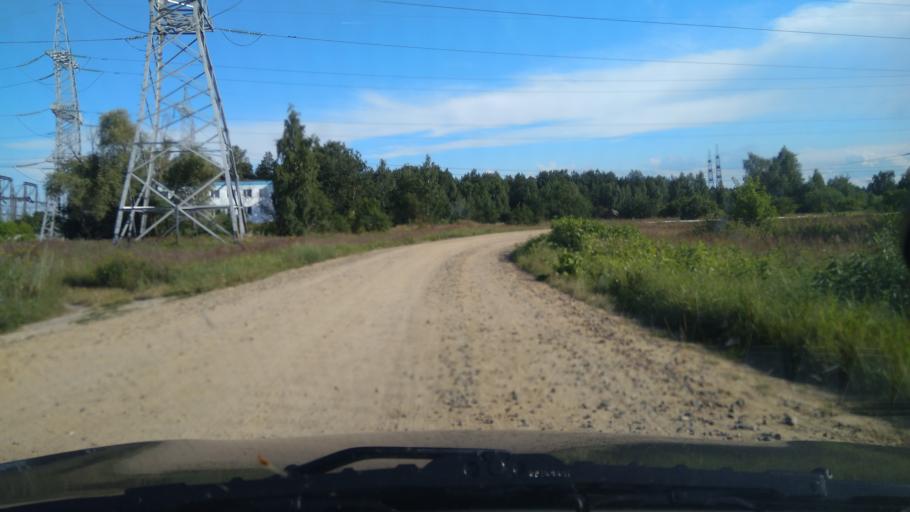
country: BY
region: Brest
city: Byelaazyorsk
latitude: 52.4550
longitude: 25.1873
